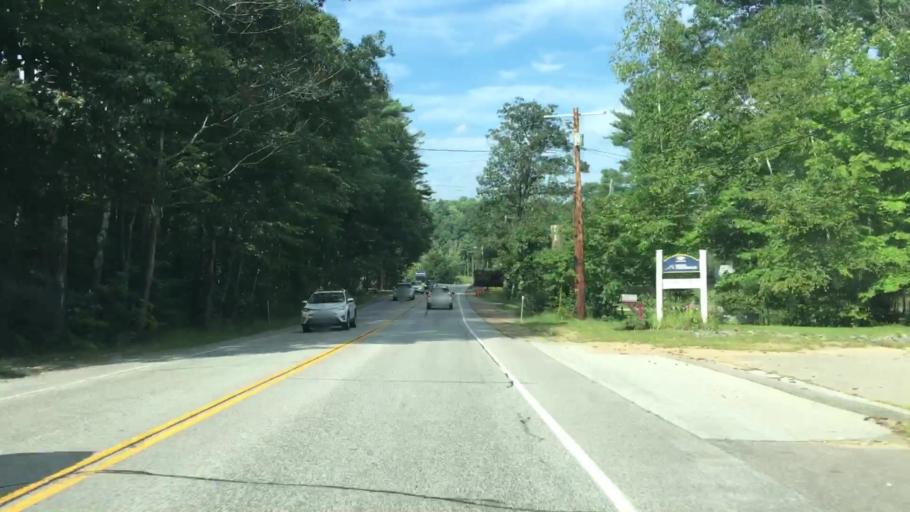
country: US
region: New Hampshire
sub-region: Belknap County
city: Sanbornton
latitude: 43.4894
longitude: -71.5276
